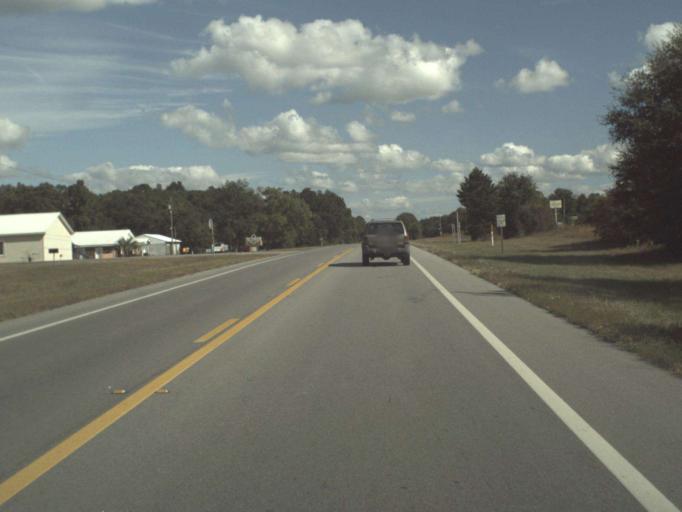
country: US
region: Florida
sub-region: Walton County
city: DeFuniak Springs
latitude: 30.7413
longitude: -86.1889
